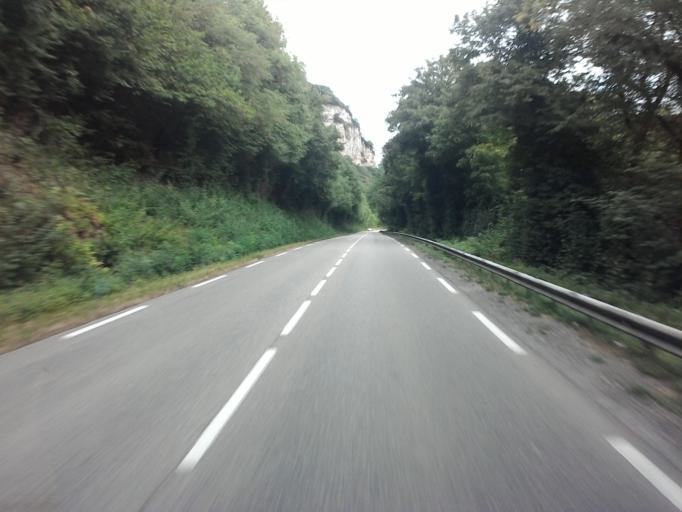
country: FR
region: Rhone-Alpes
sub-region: Departement de l'Ain
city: Saint-Sorlin-en-Bugey
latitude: 45.8639
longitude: 5.3836
